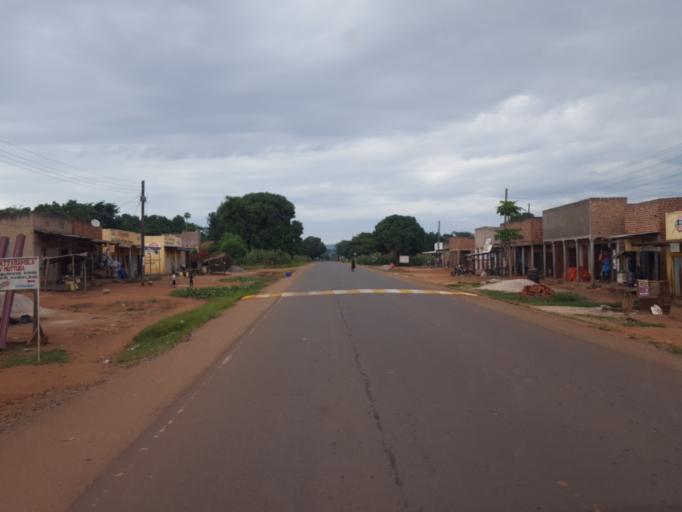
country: UG
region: Central Region
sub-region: Kiboga District
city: Kiboga
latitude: 1.0282
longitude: 31.6805
